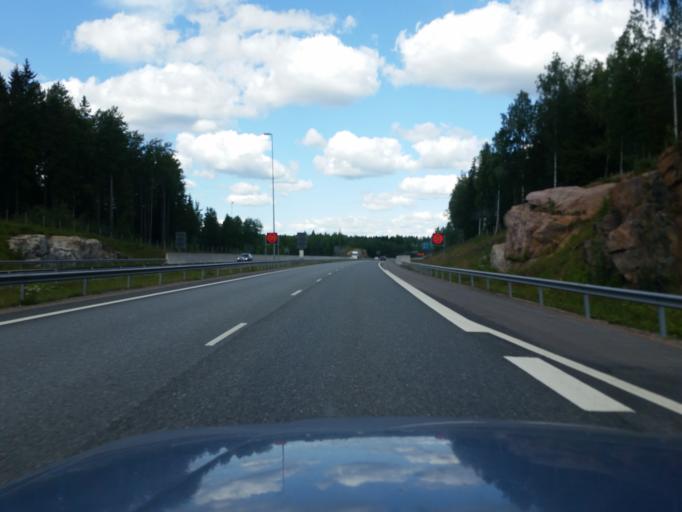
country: FI
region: Uusimaa
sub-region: Helsinki
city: Sammatti
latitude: 60.3466
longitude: 23.9035
